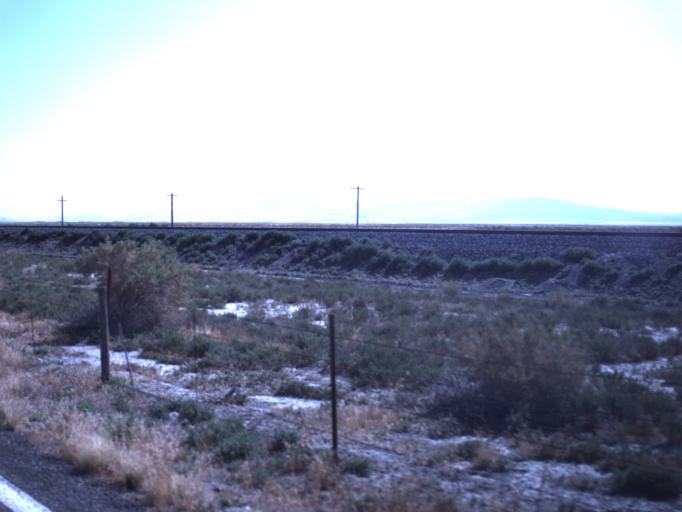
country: US
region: Utah
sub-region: Millard County
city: Delta
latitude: 39.1921
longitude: -112.6930
